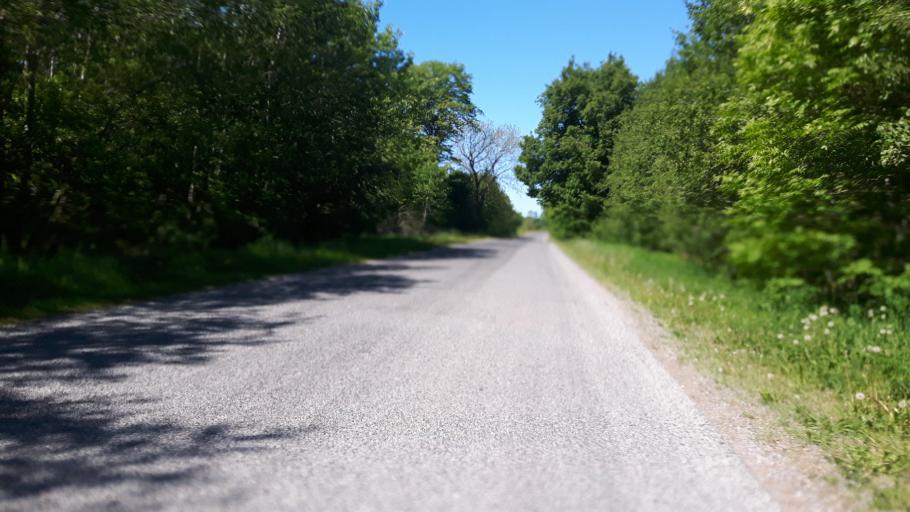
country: EE
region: Ida-Virumaa
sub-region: Sillamaee linn
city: Sillamae
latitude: 59.3770
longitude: 27.8363
